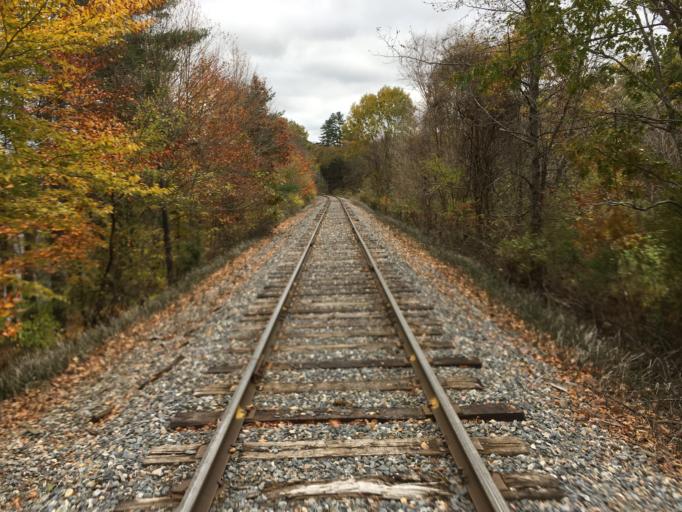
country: US
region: New Hampshire
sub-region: Grafton County
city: Woodsville
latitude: 44.1700
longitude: -72.0542
